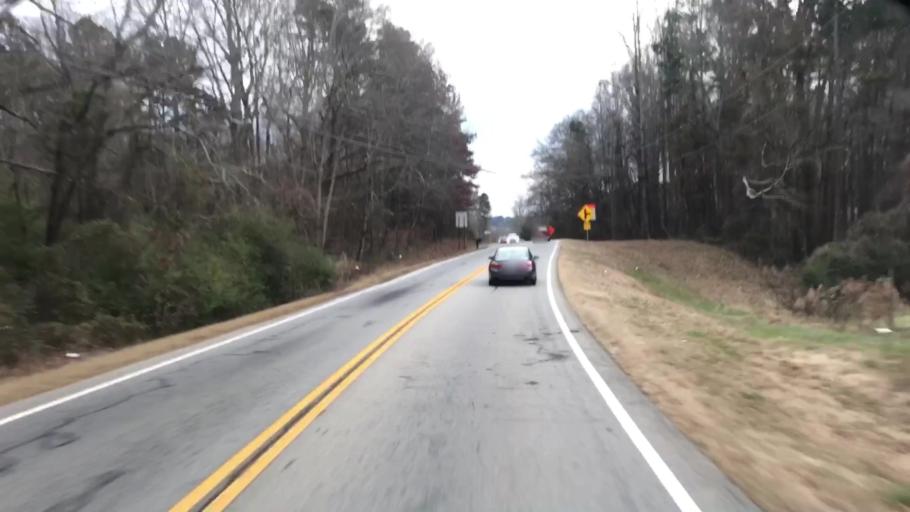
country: US
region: Georgia
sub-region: Barrow County
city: Winder
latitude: 34.0194
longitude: -83.7616
